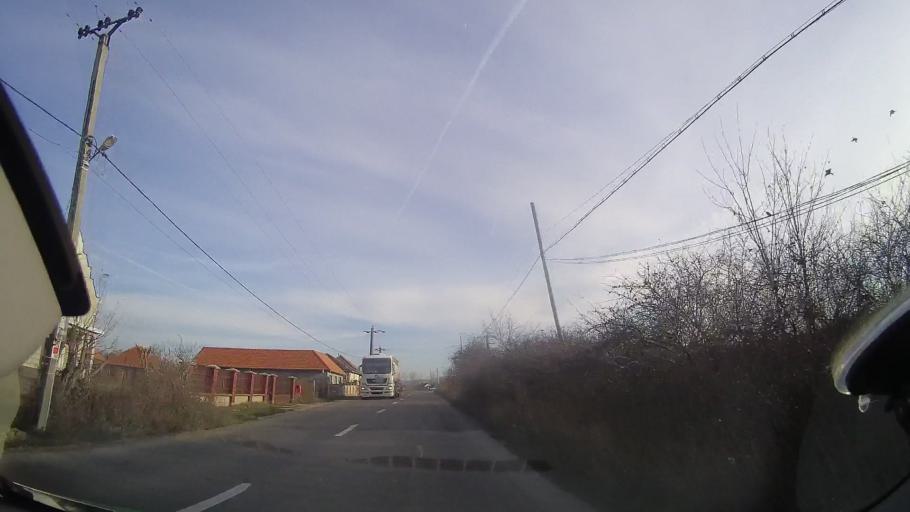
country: RO
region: Bihor
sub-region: Comuna Tileagd
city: Tileagd
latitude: 47.0673
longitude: 22.2101
